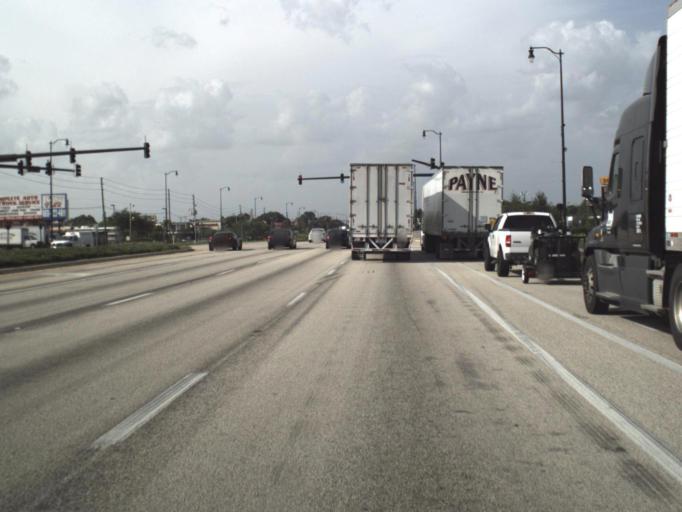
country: US
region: Florida
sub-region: Polk County
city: Haines City
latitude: 28.1168
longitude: -81.6396
